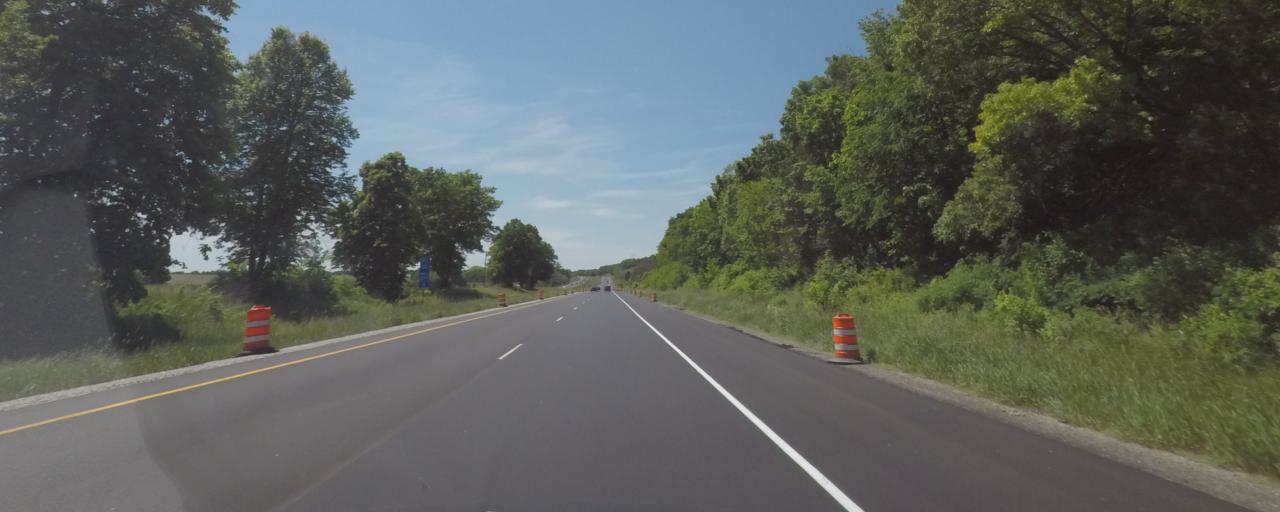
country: US
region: Wisconsin
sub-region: Jefferson County
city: Lake Mills
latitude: 43.1055
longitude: -88.9439
